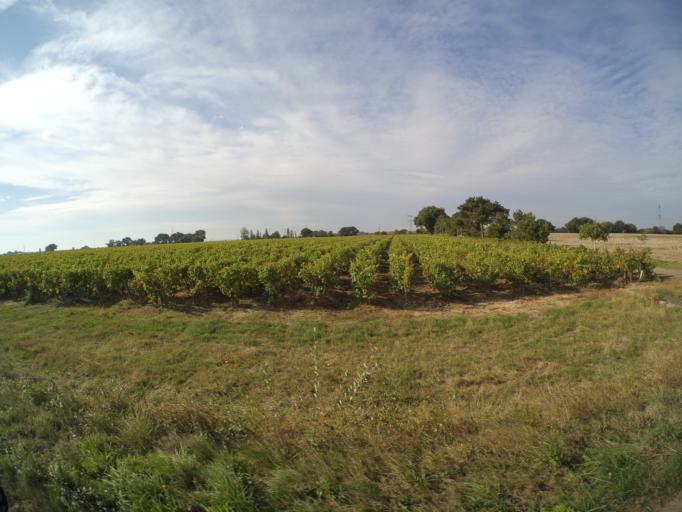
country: FR
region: Pays de la Loire
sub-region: Departement de Maine-et-Loire
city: Saint-Crespin-sur-Moine
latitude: 47.1218
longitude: -1.2198
